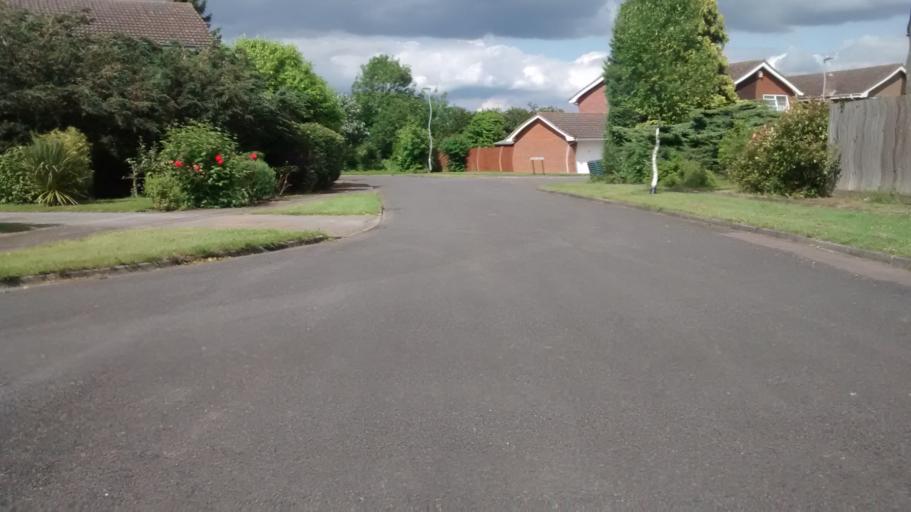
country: GB
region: England
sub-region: Cambridgeshire
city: Grantchester
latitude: 52.2018
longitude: 0.0950
